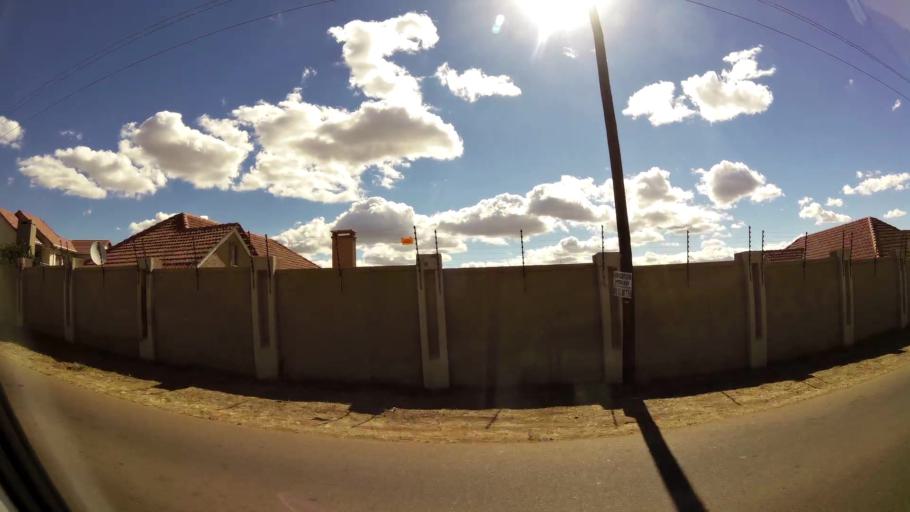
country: ZA
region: Limpopo
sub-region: Capricorn District Municipality
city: Polokwane
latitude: -23.8791
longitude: 29.5152
